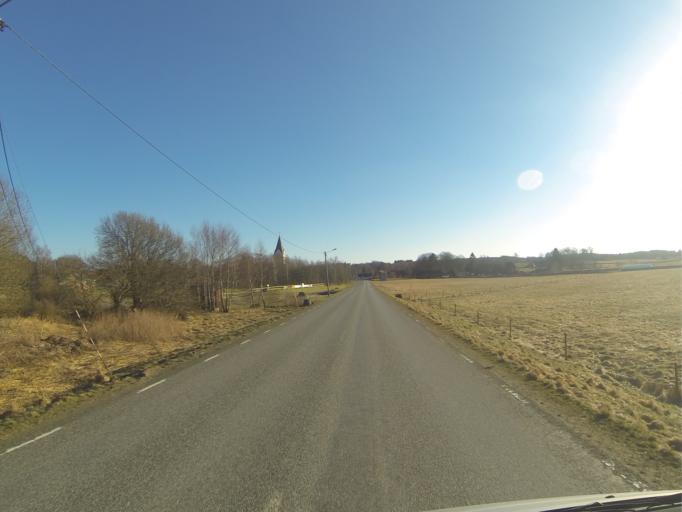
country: SE
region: Skane
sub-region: Horby Kommun
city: Hoerby
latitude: 55.9275
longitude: 13.6683
